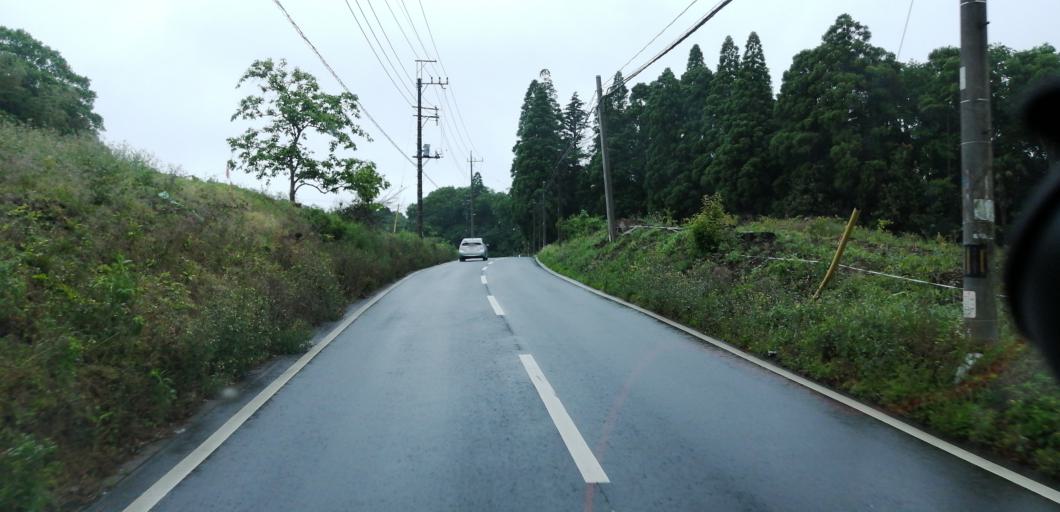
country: JP
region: Chiba
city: Yachimata
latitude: 35.6161
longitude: 140.2881
